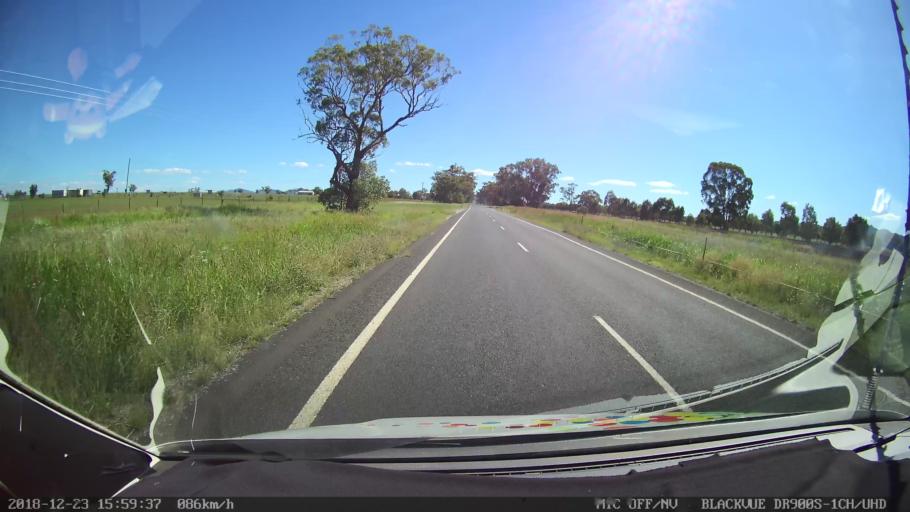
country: AU
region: New South Wales
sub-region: Tamworth Municipality
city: Phillip
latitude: -31.2017
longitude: 150.8317
